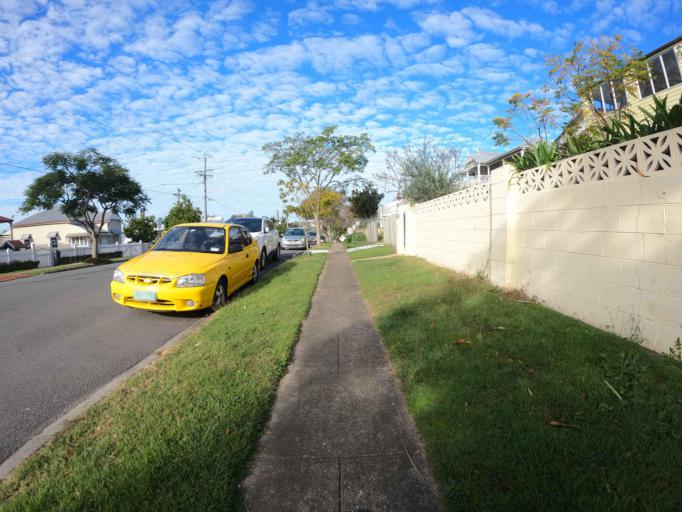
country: AU
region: Queensland
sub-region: Brisbane
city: Windsor
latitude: -27.4390
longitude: 153.0277
